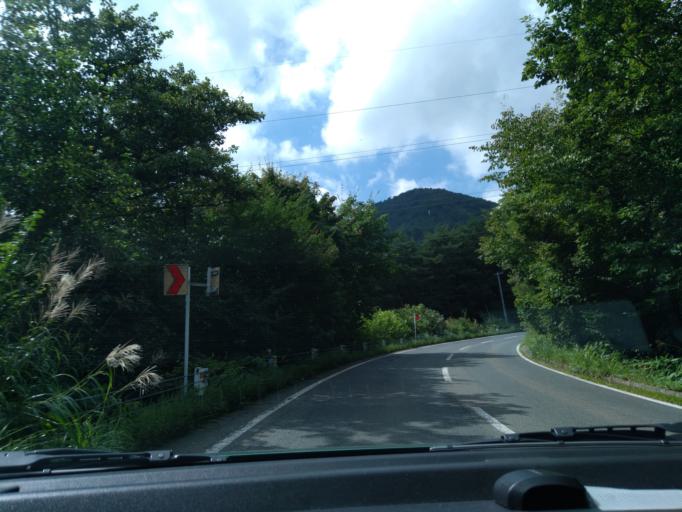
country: JP
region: Iwate
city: Morioka-shi
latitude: 39.6323
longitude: 141.0848
